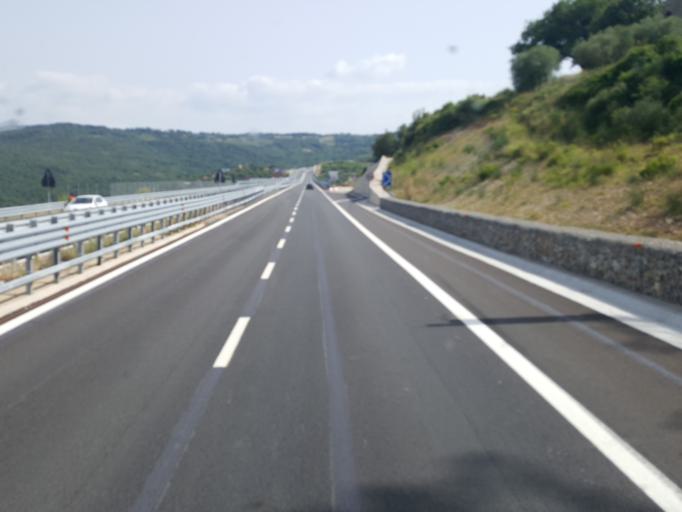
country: IT
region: Tuscany
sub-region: Provincia di Grosseto
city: Civitella Marittima
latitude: 43.0840
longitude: 11.2942
